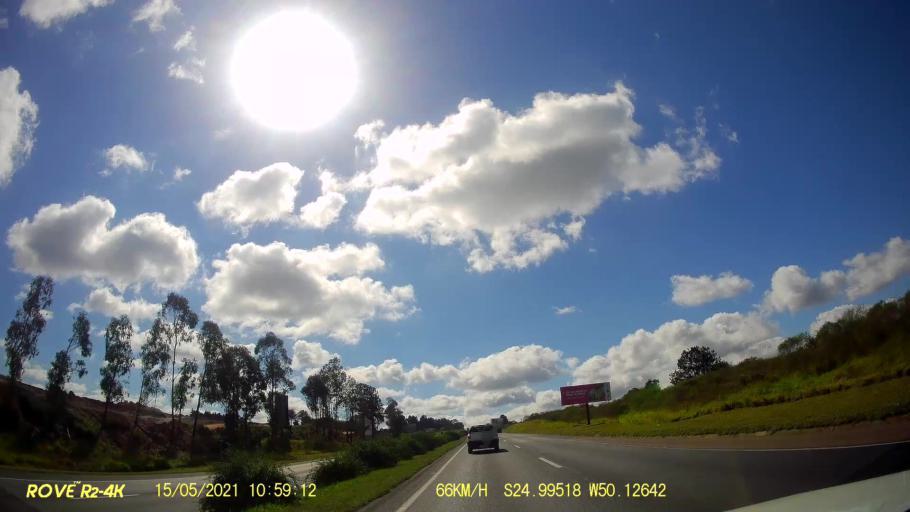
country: BR
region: Parana
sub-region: Carambei
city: Carambei
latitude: -24.9952
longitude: -50.1265
